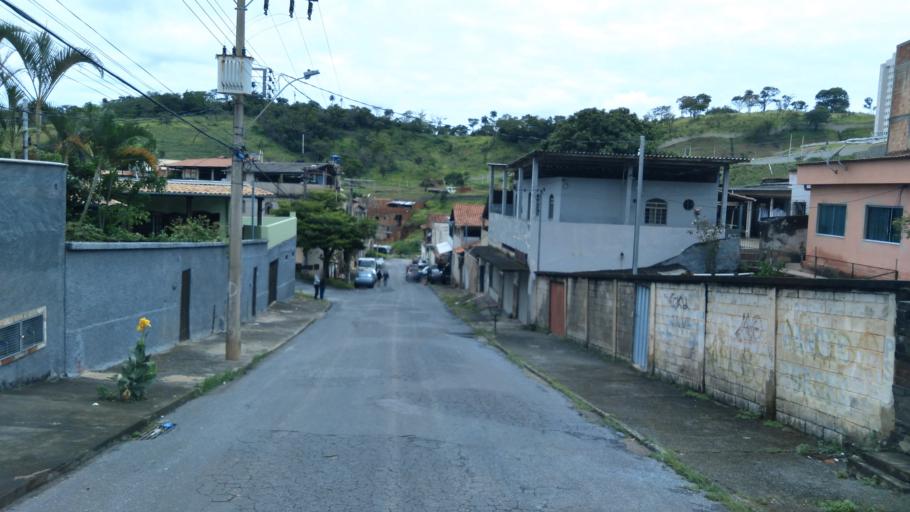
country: BR
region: Minas Gerais
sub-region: Belo Horizonte
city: Belo Horizonte
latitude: -19.8842
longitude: -43.8957
